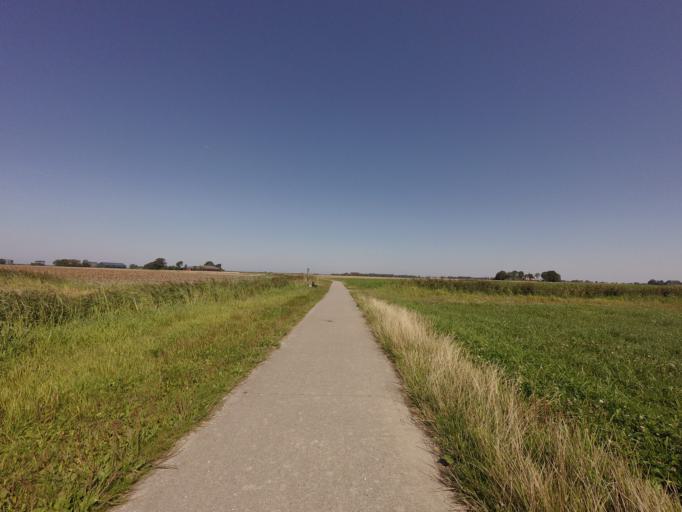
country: NL
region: Friesland
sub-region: Gemeente Dongeradeel
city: Anjum
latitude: 53.3871
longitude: 6.0656
